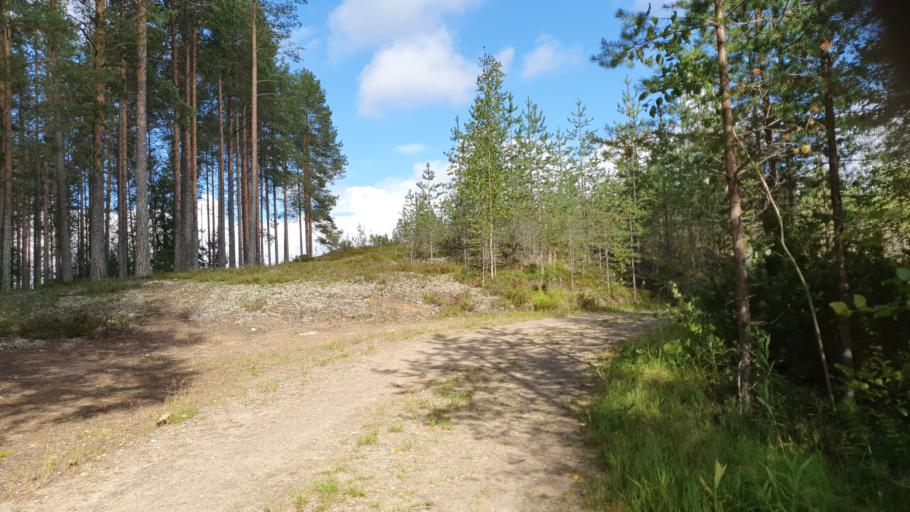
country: FI
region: Kainuu
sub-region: Kehys-Kainuu
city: Kuhmo
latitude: 64.1478
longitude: 29.3555
